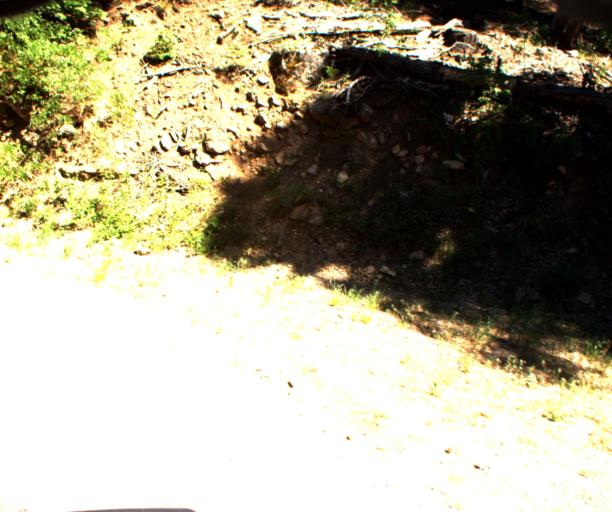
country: US
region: Arizona
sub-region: Graham County
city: Swift Trail Junction
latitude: 32.6278
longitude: -109.8226
